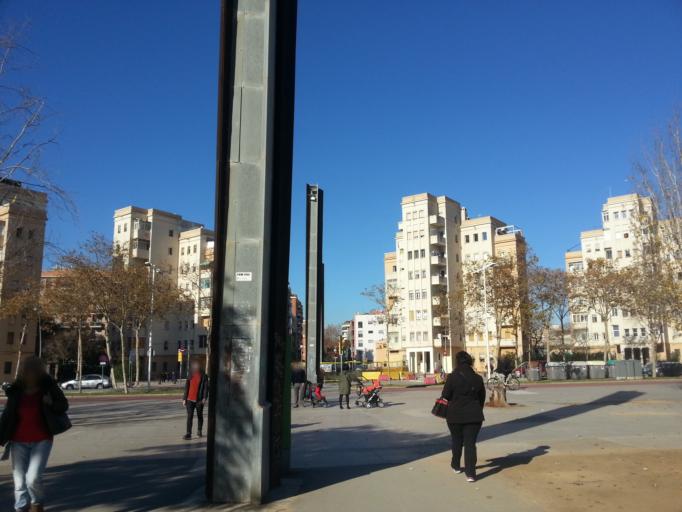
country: ES
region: Catalonia
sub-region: Provincia de Barcelona
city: Sant Marti
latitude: 41.3970
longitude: 2.2066
